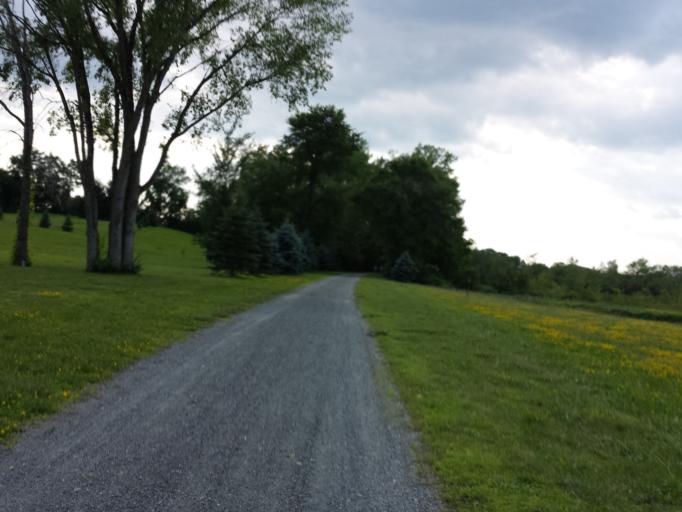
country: US
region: New York
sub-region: Saratoga County
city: Country Knolls
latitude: 42.9173
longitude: -73.7623
